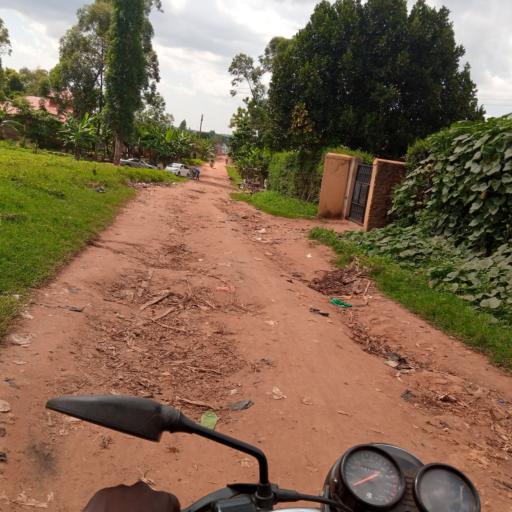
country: UG
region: Eastern Region
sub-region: Mbale District
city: Mbale
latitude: 1.1004
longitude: 34.1778
